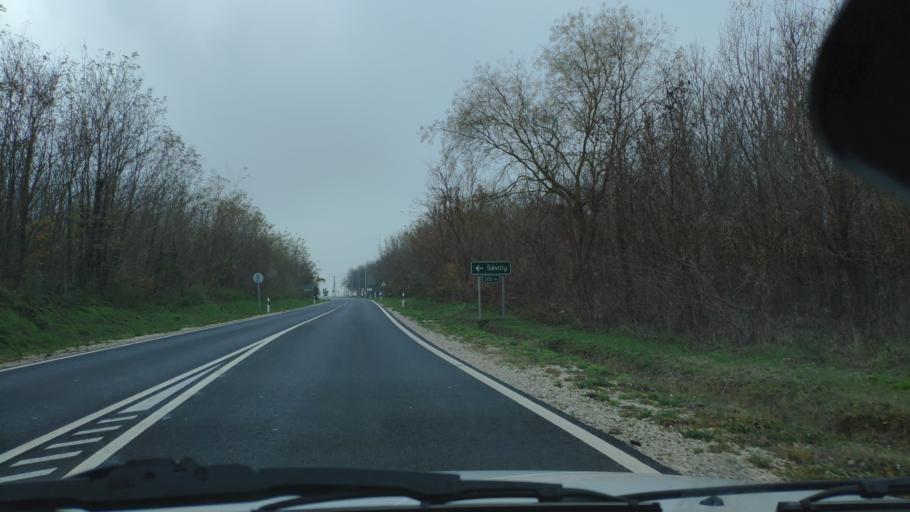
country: HU
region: Zala
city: Zalakomar
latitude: 46.6030
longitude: 17.2667
